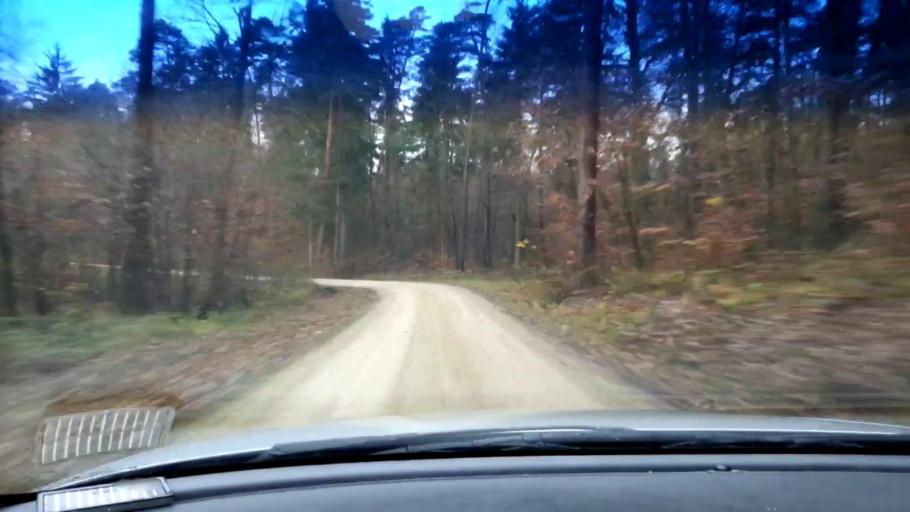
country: DE
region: Bavaria
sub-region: Upper Franconia
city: Gundelsheim
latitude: 49.9438
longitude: 10.9412
